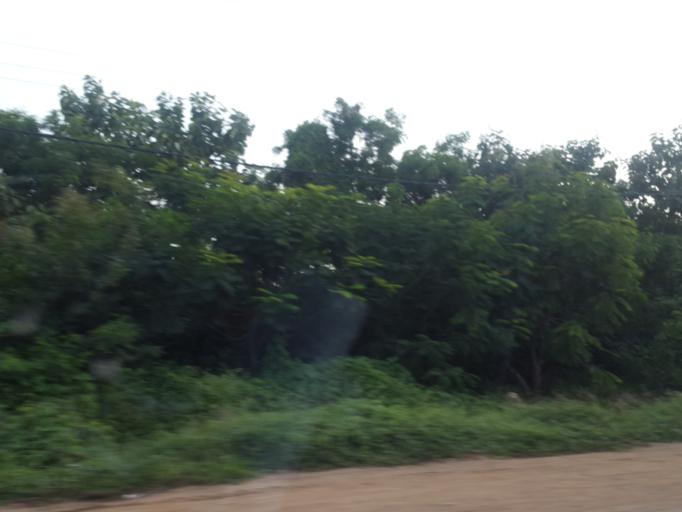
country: IN
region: Telangana
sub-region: Rangareddi
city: Kukatpalli
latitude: 17.5417
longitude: 78.3874
